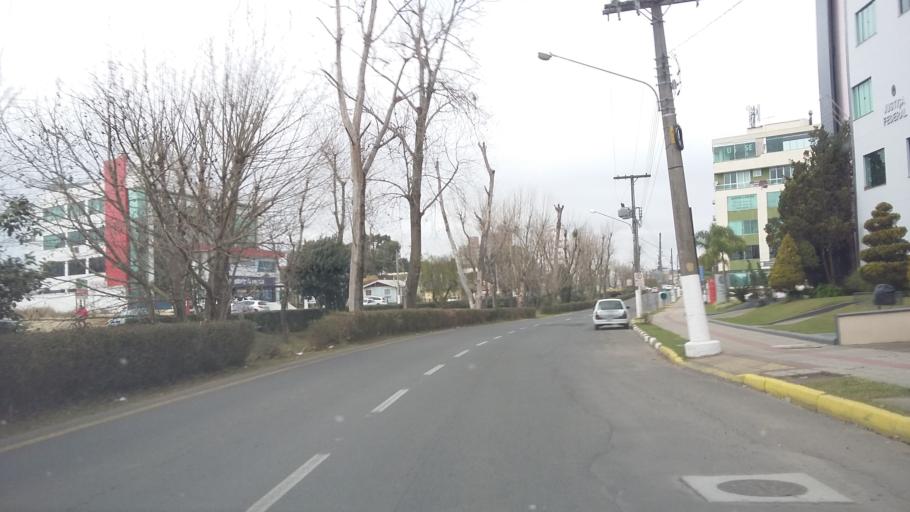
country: BR
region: Santa Catarina
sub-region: Lages
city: Lages
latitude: -27.8086
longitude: -50.3187
